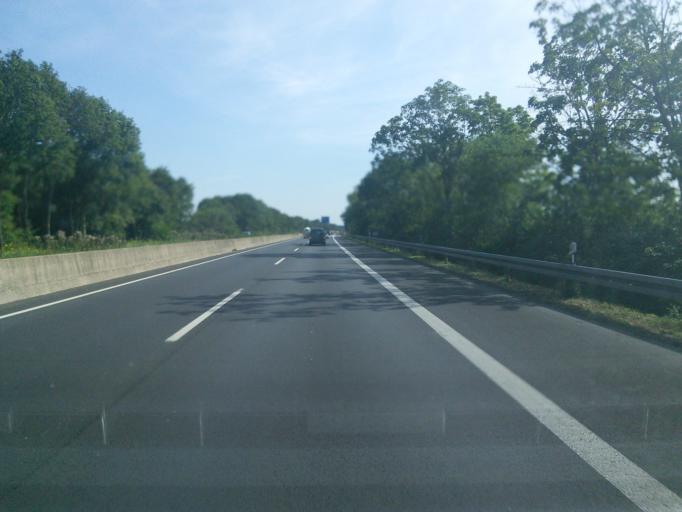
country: DE
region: North Rhine-Westphalia
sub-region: Regierungsbezirk Dusseldorf
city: Dormagen
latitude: 51.0611
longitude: 6.8328
